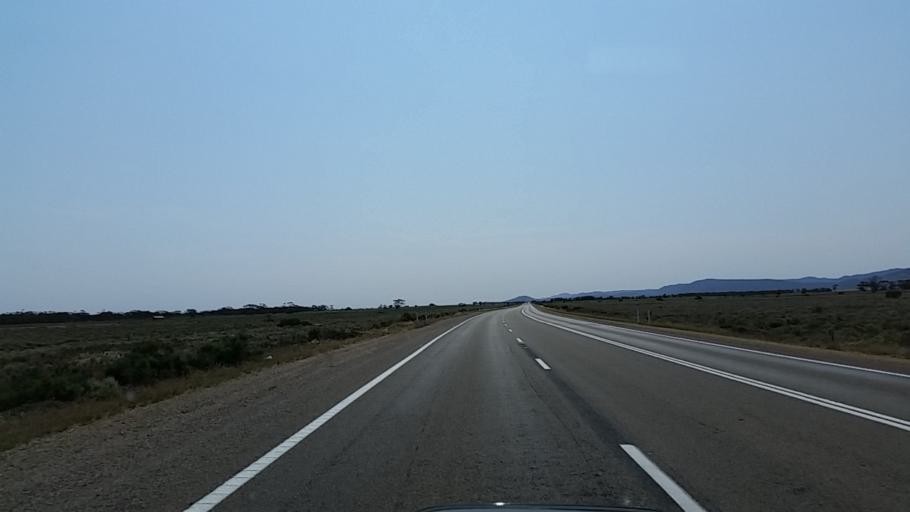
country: AU
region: South Australia
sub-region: Port Pirie City and Dists
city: Port Pirie
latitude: -32.9734
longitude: 137.9826
